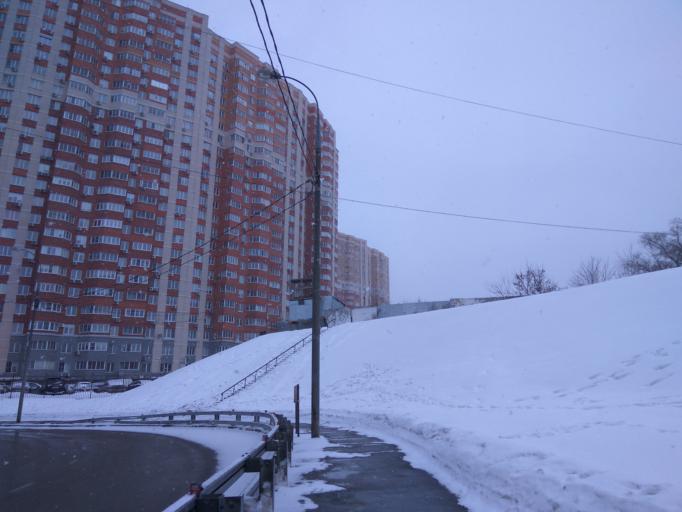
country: RU
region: Moscow
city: Strogino
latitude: 55.7925
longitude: 37.3965
